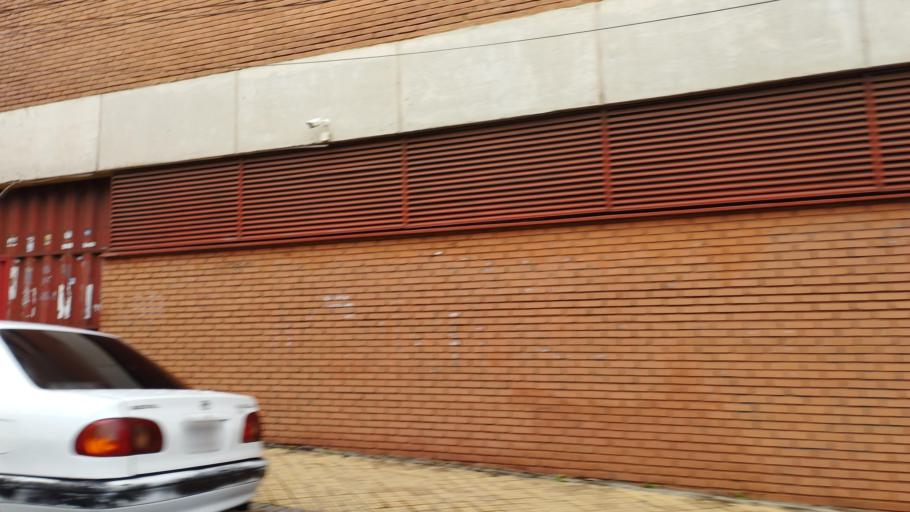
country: PY
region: Asuncion
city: Asuncion
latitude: -25.2890
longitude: -57.6357
